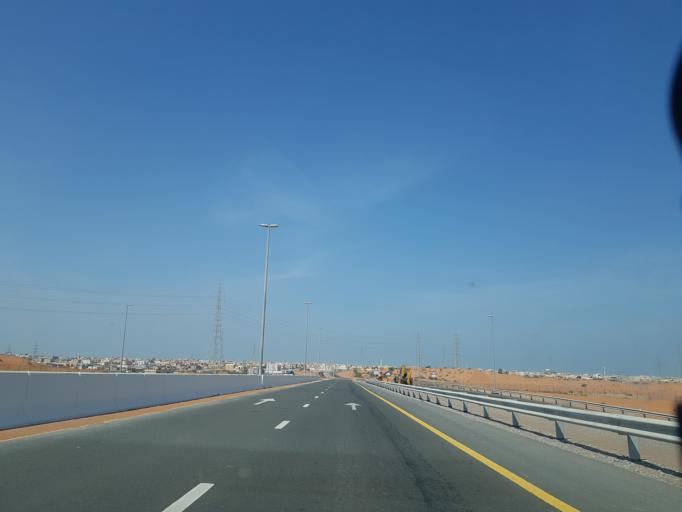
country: AE
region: Ra's al Khaymah
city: Ras al-Khaimah
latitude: 25.6958
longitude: 55.9244
